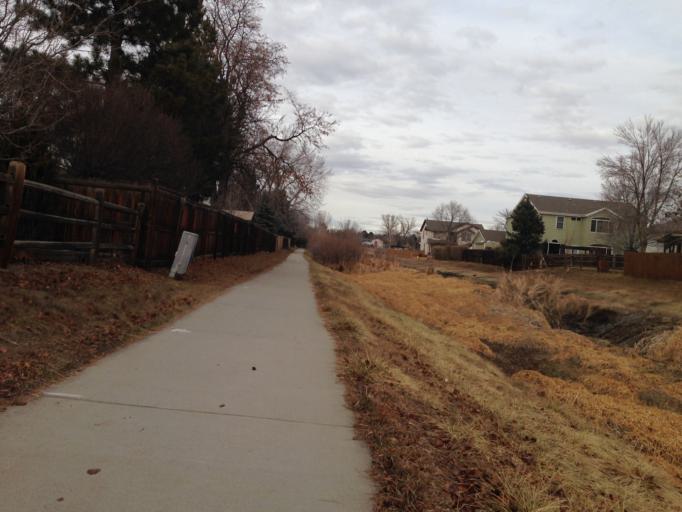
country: US
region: Colorado
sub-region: Adams County
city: Westminster
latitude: 39.8455
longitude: -105.0629
